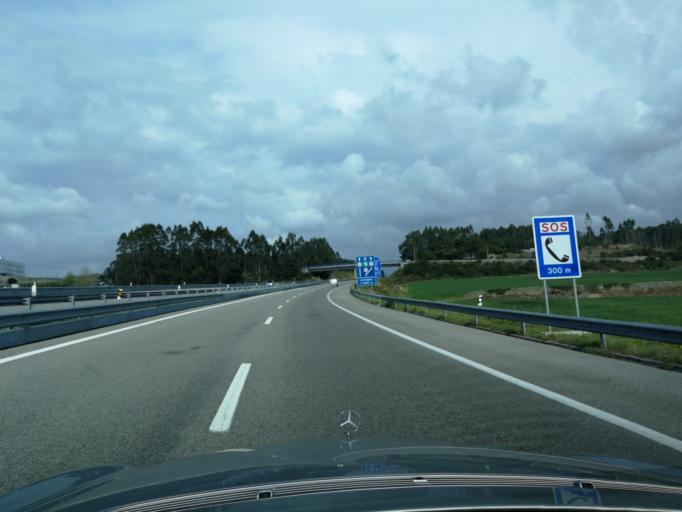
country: PT
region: Porto
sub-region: Vila do Conde
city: Vila do Conde
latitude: 41.3835
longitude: -8.7131
